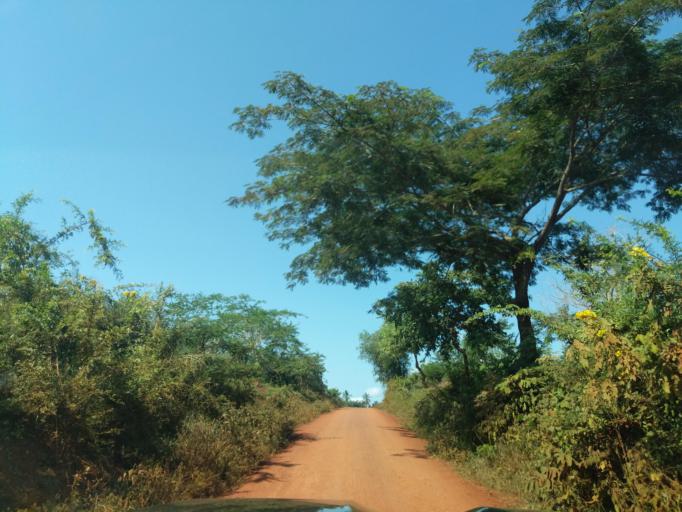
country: TZ
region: Tanga
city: Muheza
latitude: -5.3796
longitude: 38.5813
